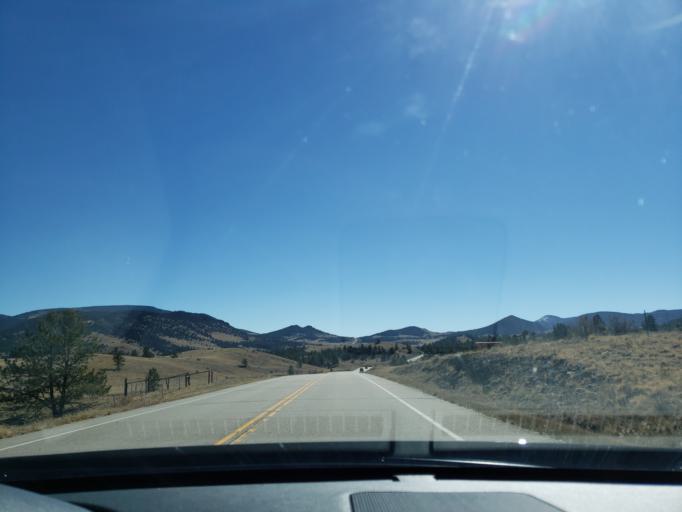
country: US
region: Colorado
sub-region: Chaffee County
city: Buena Vista
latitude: 38.8755
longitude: -105.6723
